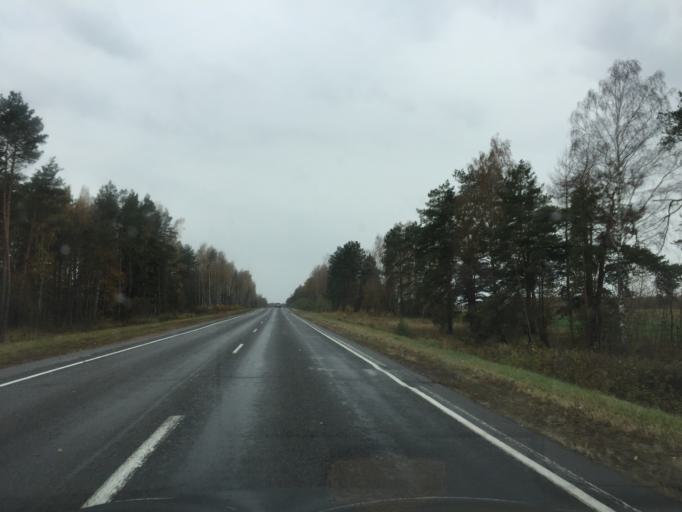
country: BY
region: Mogilev
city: Slawharad
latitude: 53.3831
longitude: 30.8869
